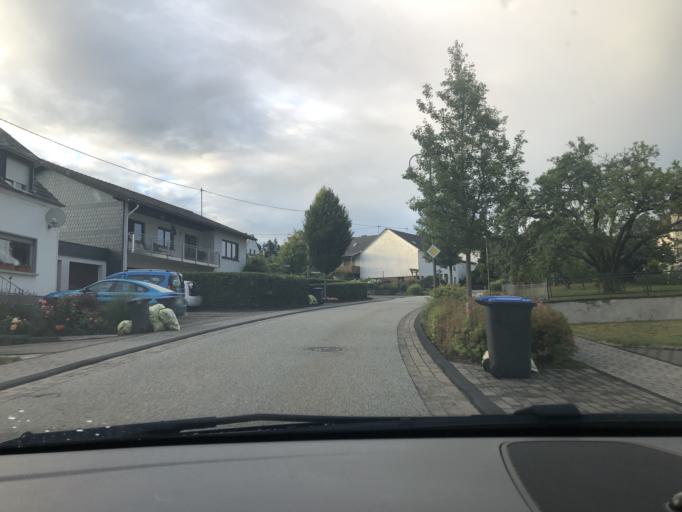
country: DE
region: Rheinland-Pfalz
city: Gusenburg
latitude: 49.6376
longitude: 6.8996
